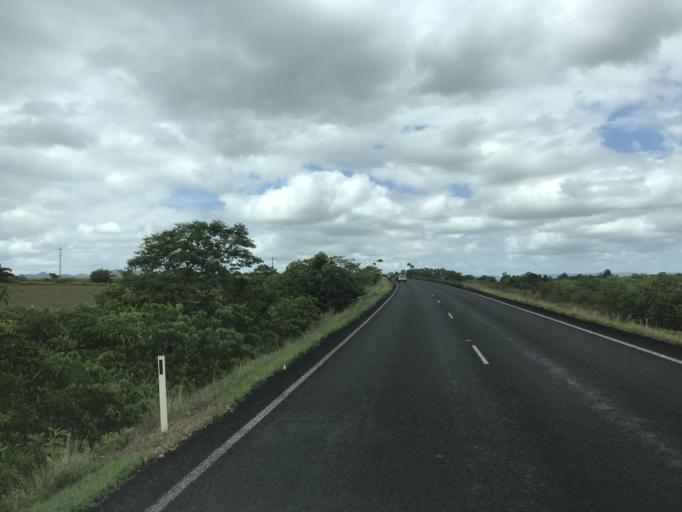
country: AU
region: Queensland
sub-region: Cassowary Coast
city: Innisfail
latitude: -17.5780
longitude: 145.9738
